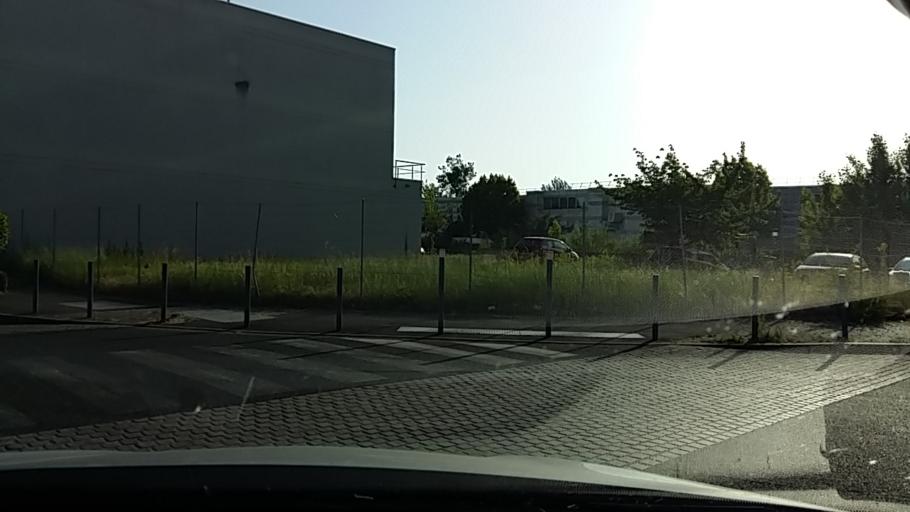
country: FR
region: Ile-de-France
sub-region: Departement du Val-de-Marne
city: Boissy-Saint-Leger
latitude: 48.7722
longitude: 2.5058
